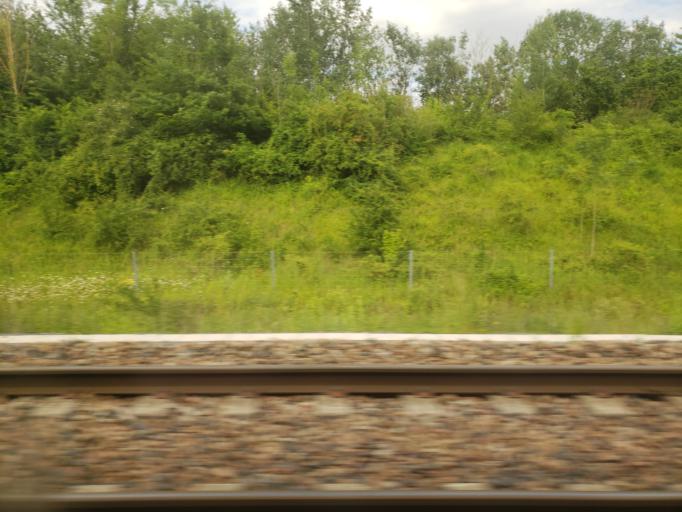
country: FR
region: Ile-de-France
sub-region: Departement de Seine-et-Marne
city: Serris
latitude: 48.8174
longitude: 2.7844
